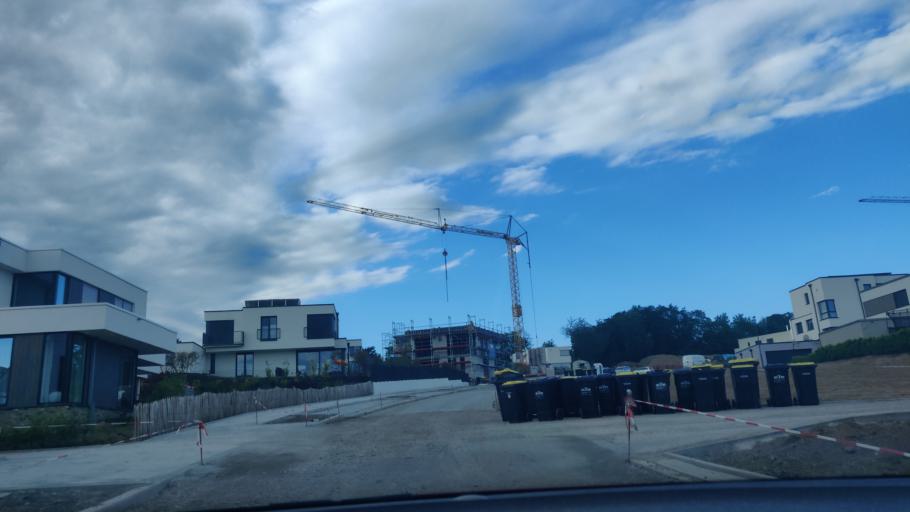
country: DE
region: North Rhine-Westphalia
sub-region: Regierungsbezirk Dusseldorf
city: Velbert
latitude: 51.3808
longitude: 7.0098
